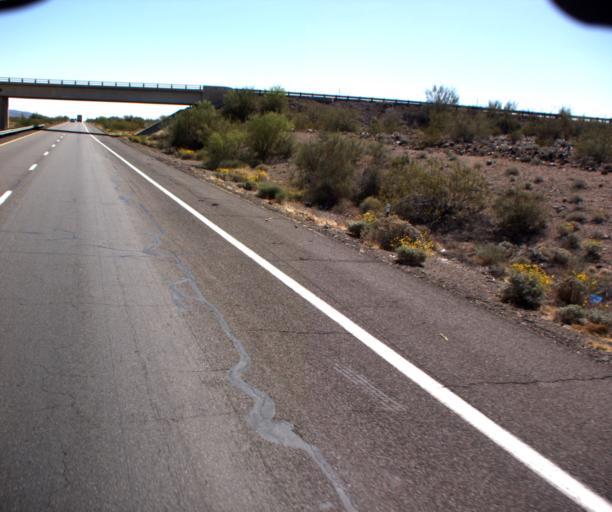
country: US
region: Arizona
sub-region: La Paz County
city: Quartzsite
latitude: 33.6616
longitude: -114.0120
